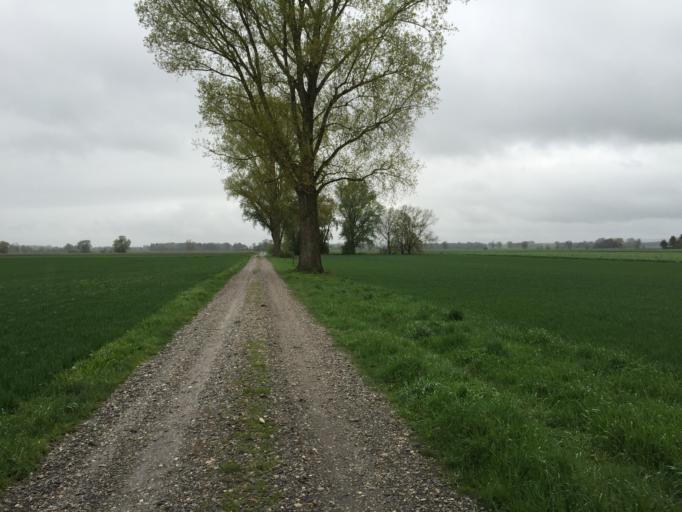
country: DE
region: Bavaria
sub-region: Swabia
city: Binswangen
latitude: 48.5742
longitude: 10.6546
